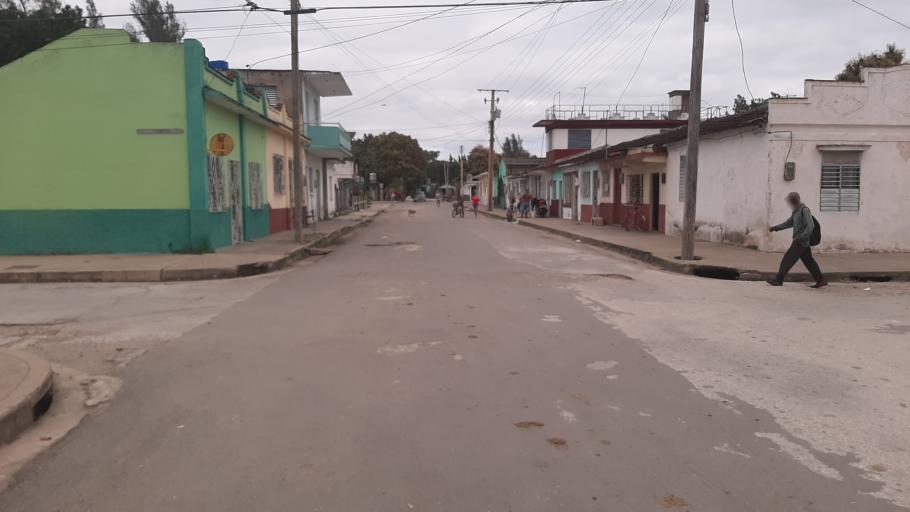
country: CU
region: Cienfuegos
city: Cruces
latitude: 22.3427
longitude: -80.2747
